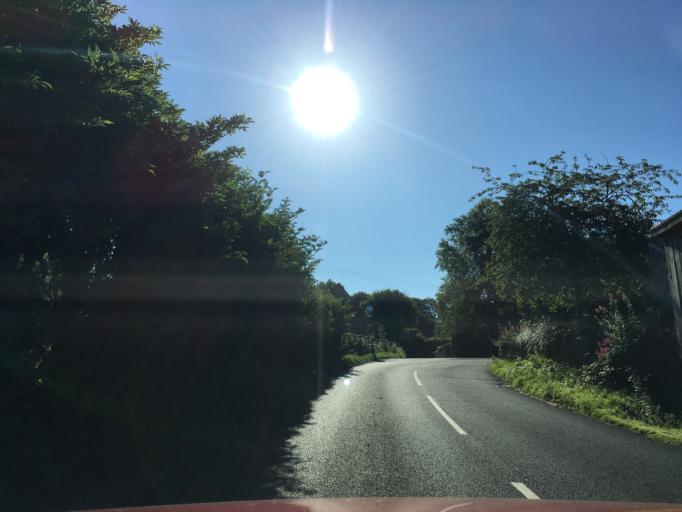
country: GB
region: England
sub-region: Gloucestershire
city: Coleford
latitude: 51.7918
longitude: -2.6485
